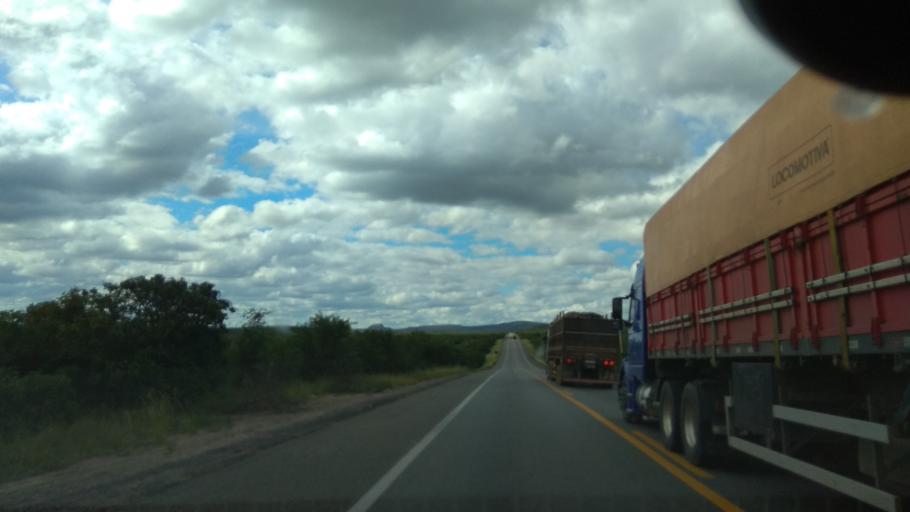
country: BR
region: Bahia
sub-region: Amargosa
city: Amargosa
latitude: -12.9541
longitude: -39.9203
